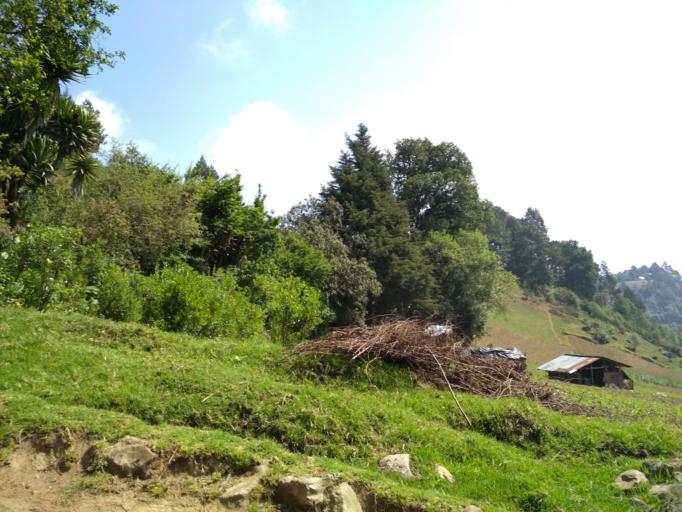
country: MX
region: Veracruz
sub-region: Mariano Escobedo
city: San Isidro el Berro
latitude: 18.9435
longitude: -97.2184
